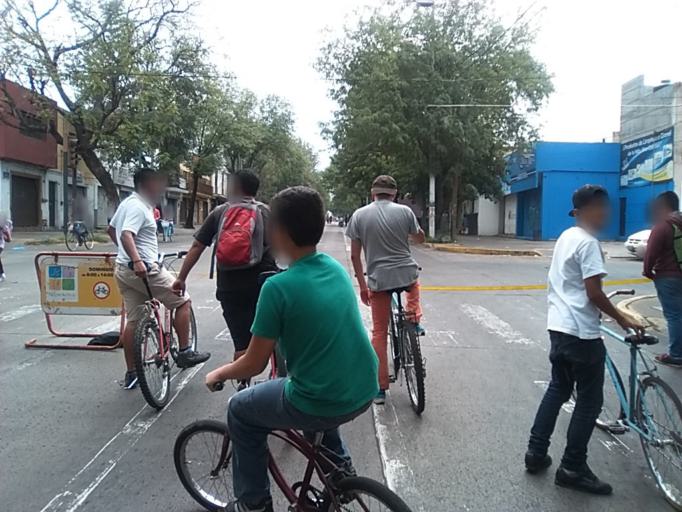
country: MX
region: Jalisco
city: Tlaquepaque
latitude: 20.6718
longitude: -103.3281
